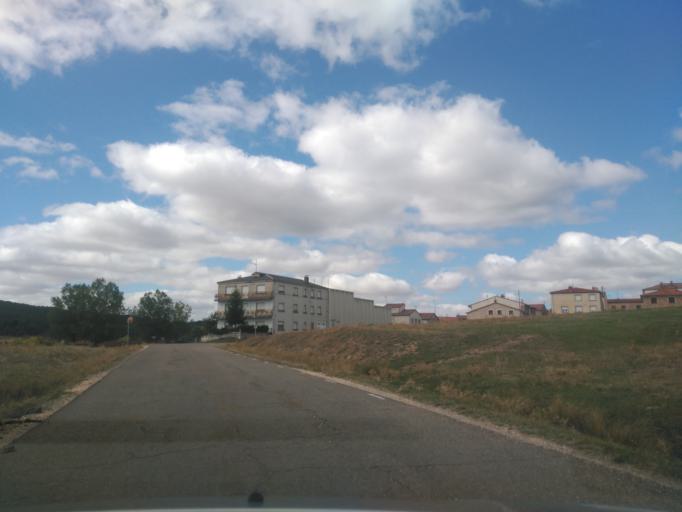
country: ES
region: Castille and Leon
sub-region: Provincia de Soria
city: Espejon
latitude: 41.8543
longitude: -3.2234
